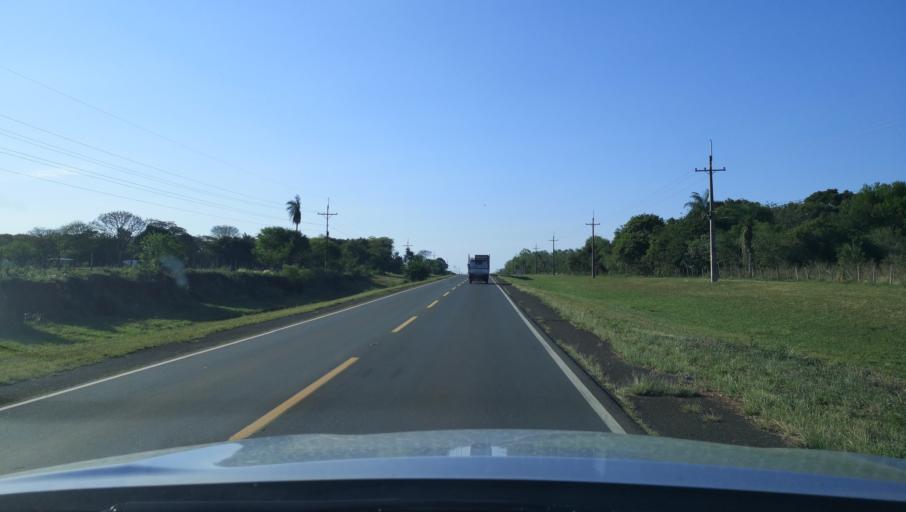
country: PY
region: Misiones
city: Santa Maria
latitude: -26.7696
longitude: -57.0311
